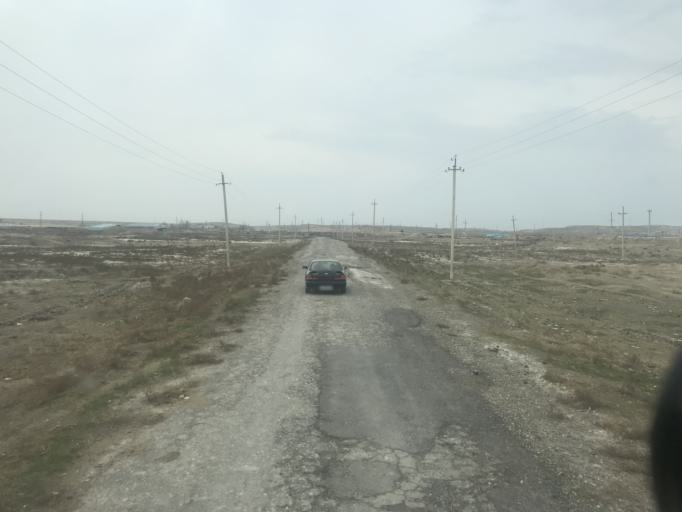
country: KZ
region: Ongtustik Qazaqstan
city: Shardara
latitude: 41.2589
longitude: 67.9328
